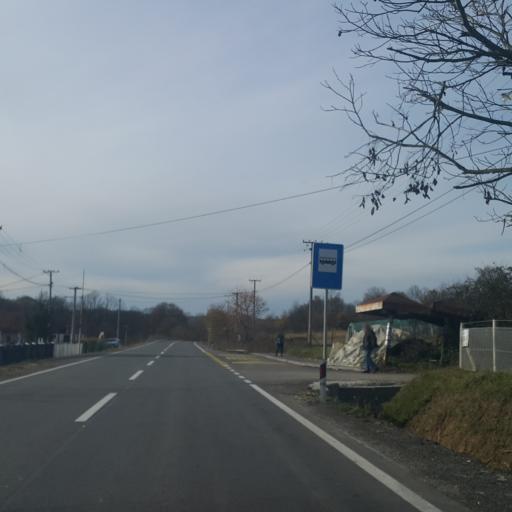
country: RS
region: Central Serbia
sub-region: Sumadijski Okrug
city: Arangelovac
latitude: 44.3430
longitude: 20.4109
